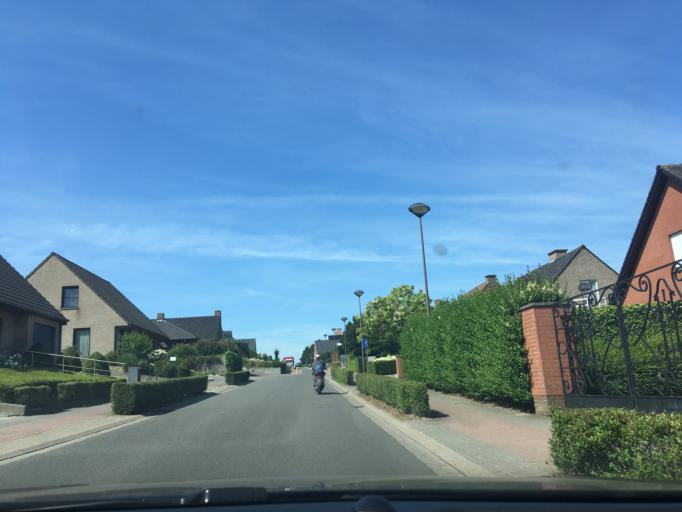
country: BE
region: Flanders
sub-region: Provincie West-Vlaanderen
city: Tielt
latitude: 50.9907
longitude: 3.3150
